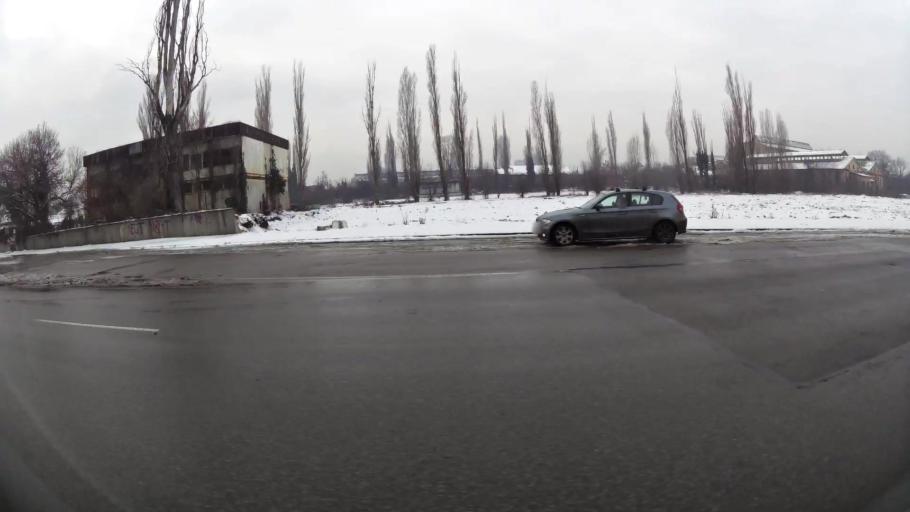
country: BG
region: Sofia-Capital
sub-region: Stolichna Obshtina
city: Sofia
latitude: 42.7136
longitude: 23.3286
